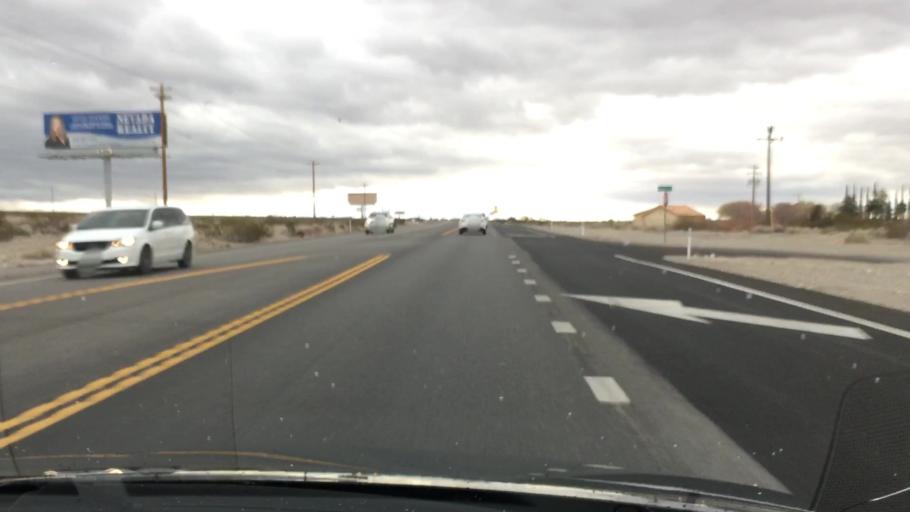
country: US
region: Nevada
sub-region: Nye County
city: Pahrump
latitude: 36.1529
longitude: -115.8969
